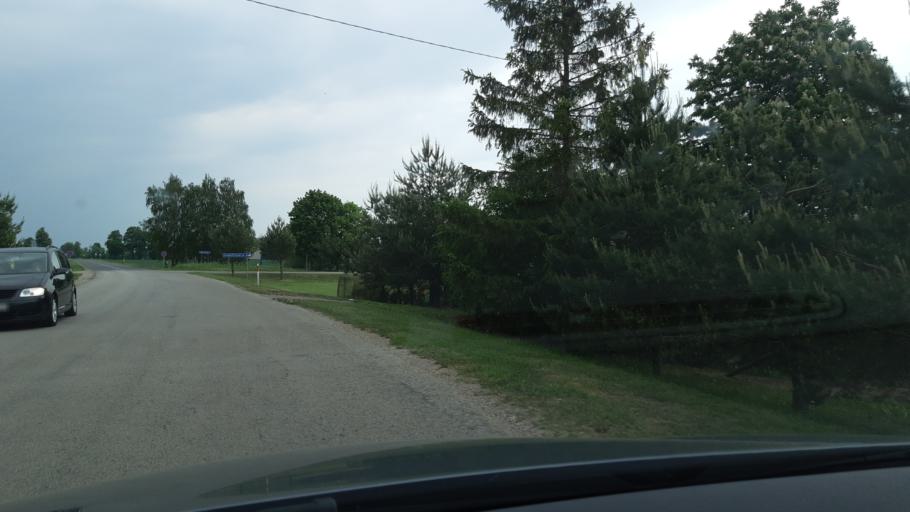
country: LT
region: Kauno apskritis
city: Kedainiai
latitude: 55.1758
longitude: 23.8746
